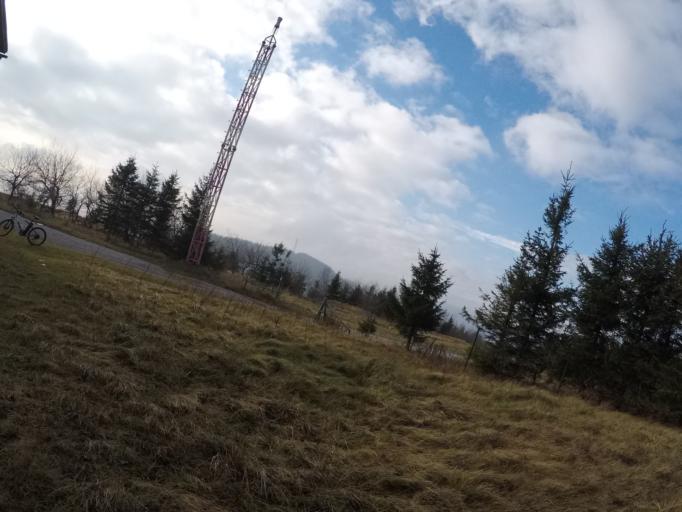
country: SK
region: Kosicky
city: Gelnica
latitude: 48.7829
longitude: 20.9869
